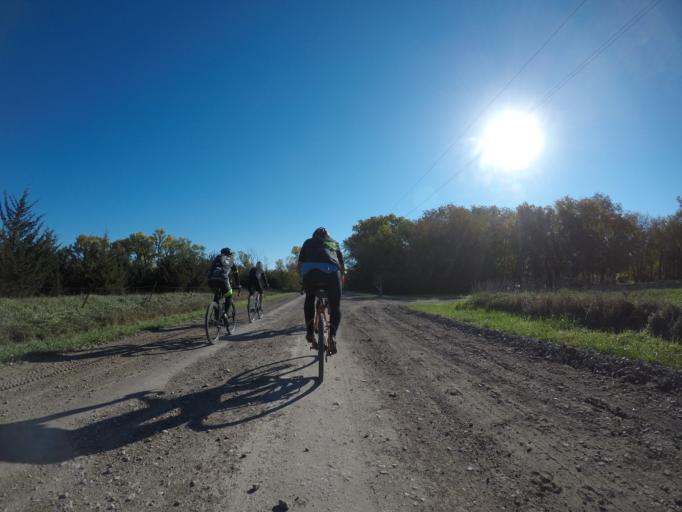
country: US
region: Kansas
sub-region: Morris County
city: Council Grove
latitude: 38.8259
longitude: -96.4777
